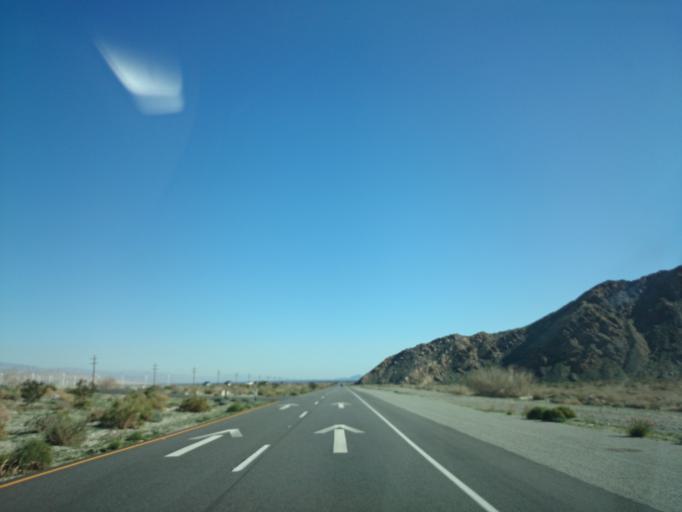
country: US
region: California
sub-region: Riverside County
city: Garnet
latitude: 33.8840
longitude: -116.5981
